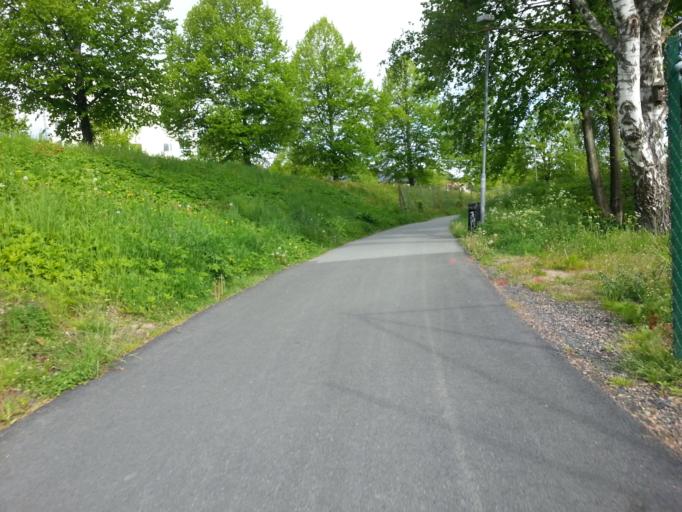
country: SE
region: Joenkoeping
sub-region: Jonkopings Kommun
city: Jonkoping
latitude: 57.7799
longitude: 14.1511
